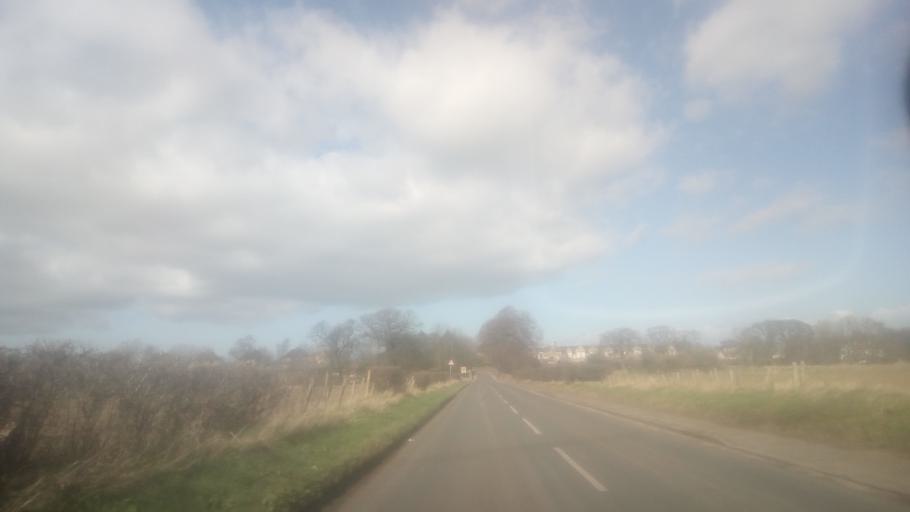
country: GB
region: Scotland
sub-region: East Lothian
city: Ormiston
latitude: 55.9084
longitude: -2.9396
